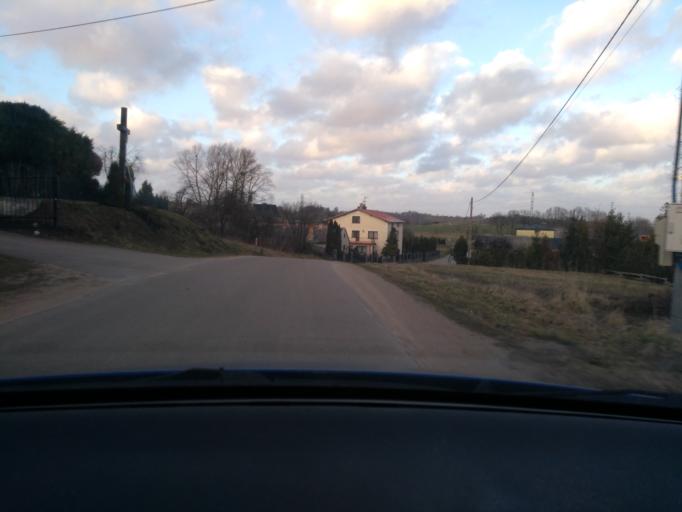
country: PL
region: Pomeranian Voivodeship
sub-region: Powiat kartuski
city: Przodkowo
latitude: 54.4177
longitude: 18.2807
